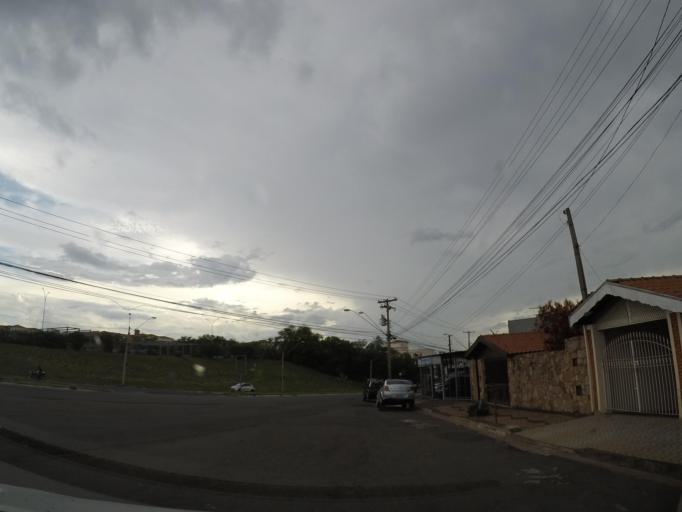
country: BR
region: Sao Paulo
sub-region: Sumare
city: Sumare
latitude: -22.8178
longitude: -47.2488
